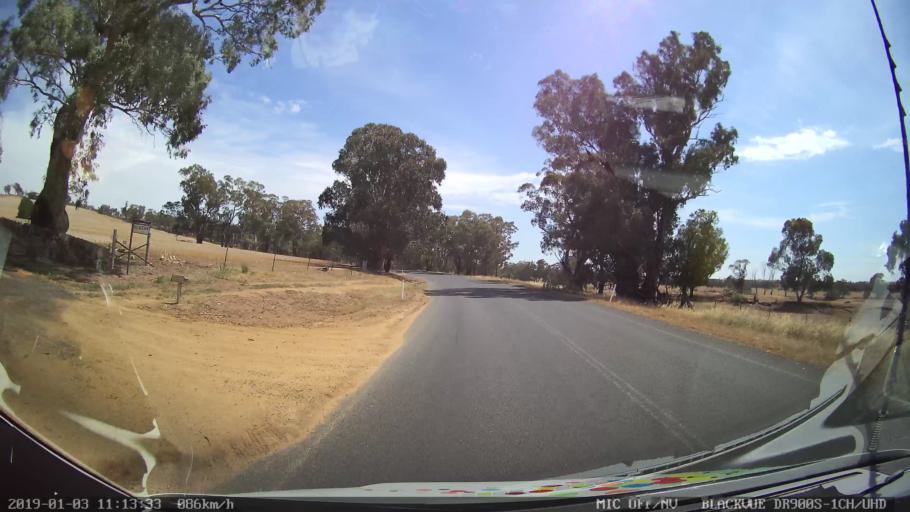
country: AU
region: New South Wales
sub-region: Young
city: Young
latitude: -34.1872
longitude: 148.2606
